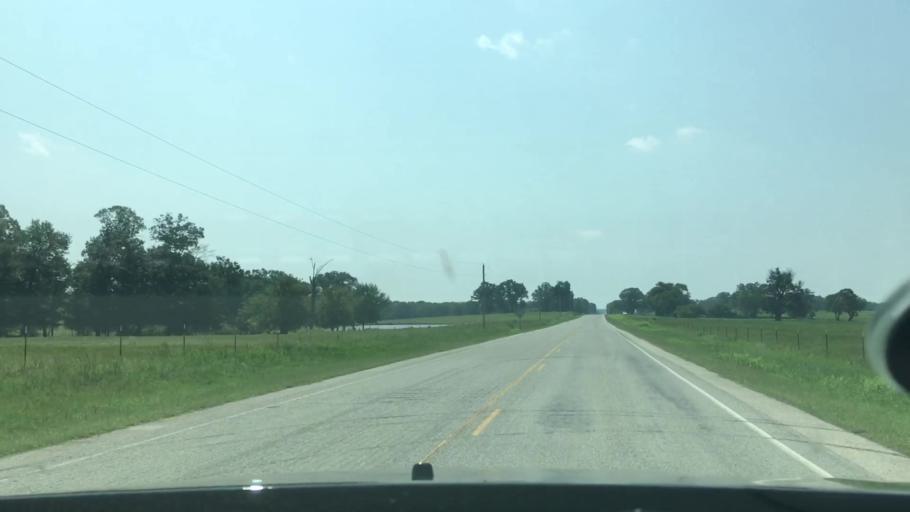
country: US
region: Oklahoma
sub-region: Atoka County
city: Atoka
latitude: 34.2769
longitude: -95.9362
